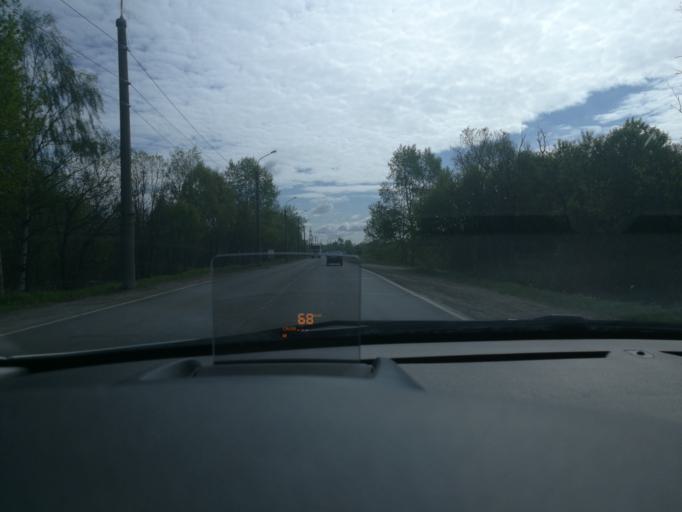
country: RU
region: Arkhangelskaya
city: Arkhangel'sk
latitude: 64.5978
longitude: 40.5325
